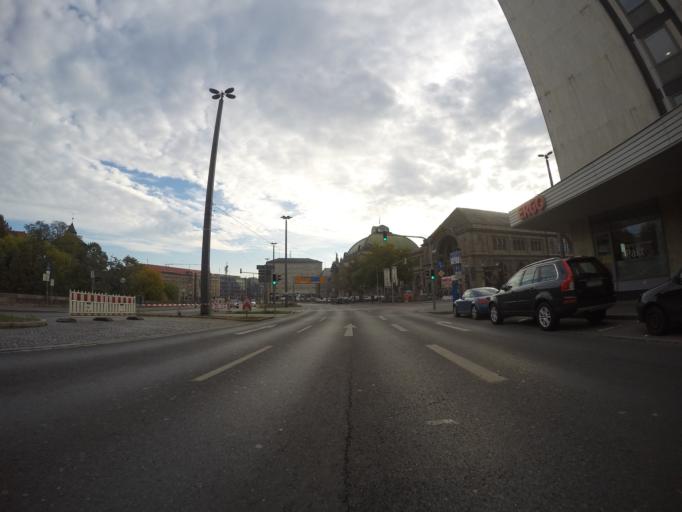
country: DE
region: Bavaria
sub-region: Regierungsbezirk Mittelfranken
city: Nuernberg
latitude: 49.4459
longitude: 11.0792
